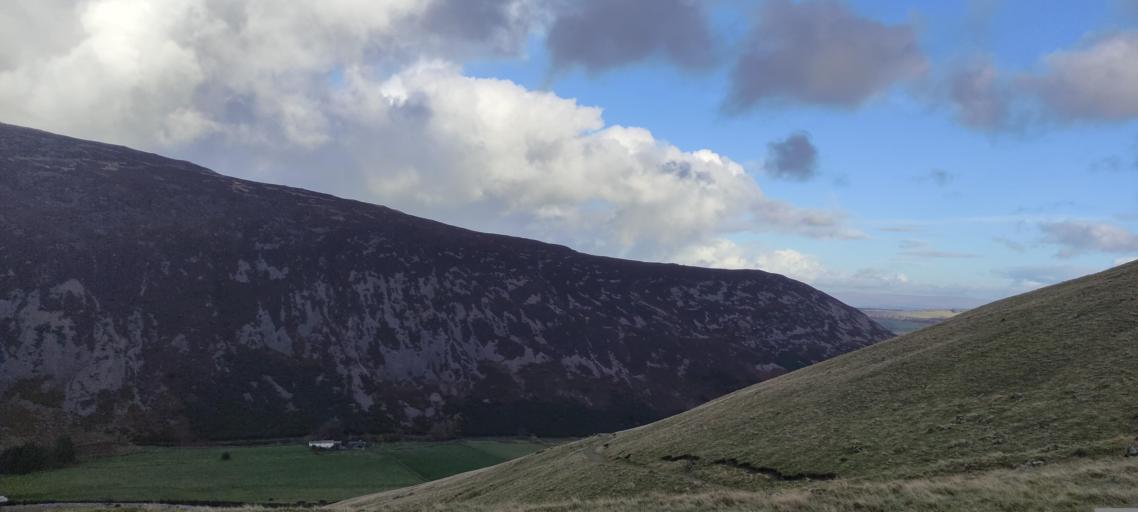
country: GB
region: England
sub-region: Cumbria
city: Keswick
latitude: 54.6756
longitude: -3.0271
